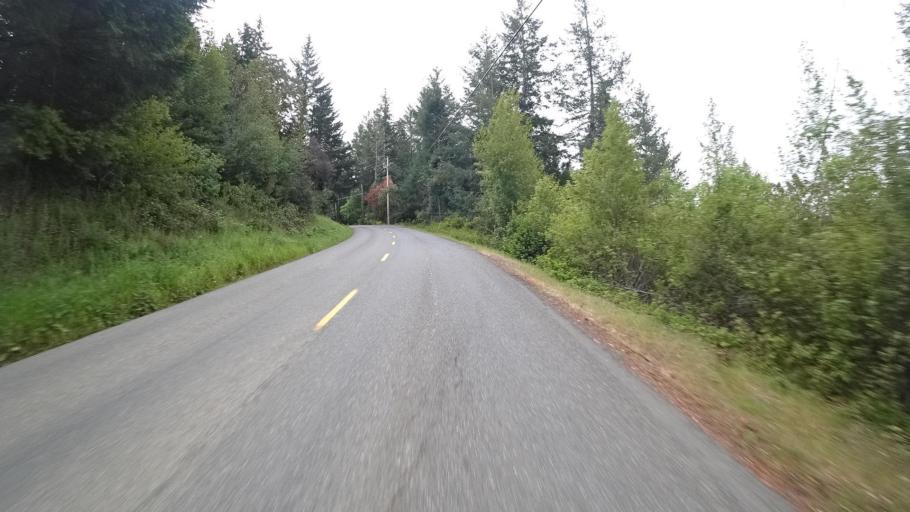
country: US
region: California
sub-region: Humboldt County
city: Redway
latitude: 40.2940
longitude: -123.8233
